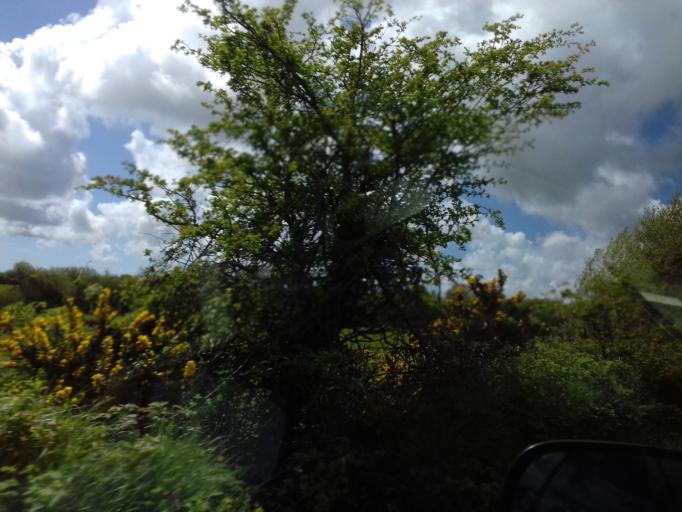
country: IE
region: Leinster
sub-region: Loch Garman
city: Loch Garman
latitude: 52.3163
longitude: -6.5228
